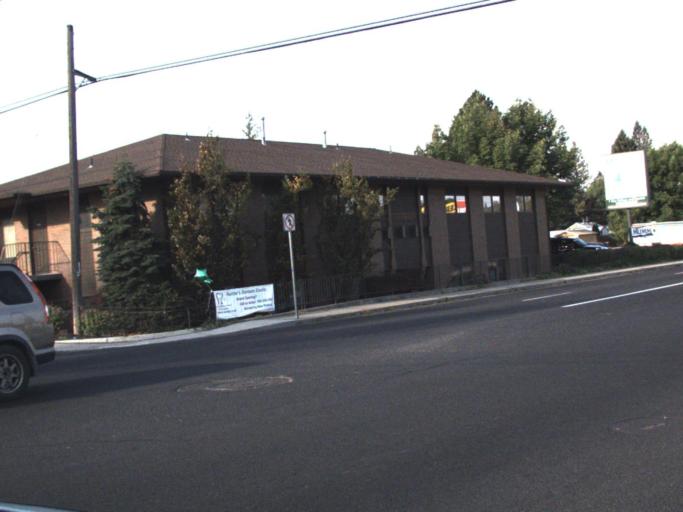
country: US
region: Washington
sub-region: Spokane County
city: Town and Country
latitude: 47.7153
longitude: -117.4276
